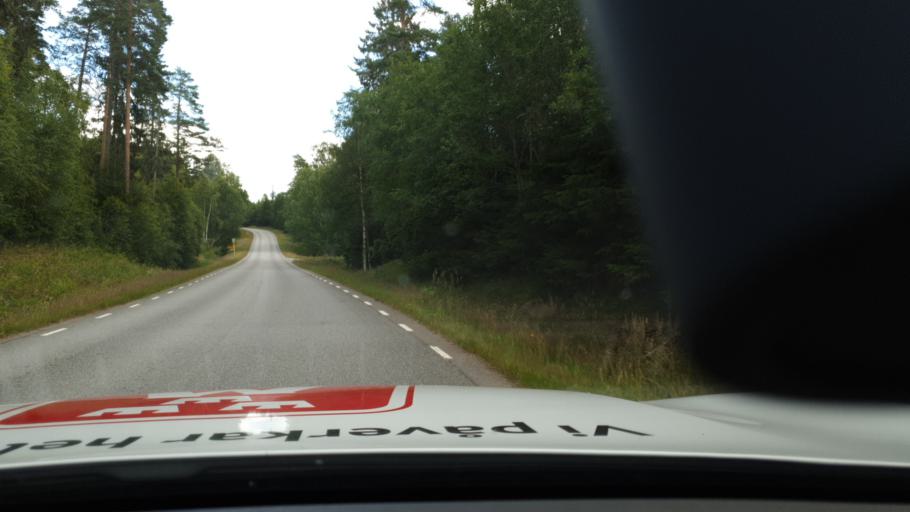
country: SE
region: Vaermland
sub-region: Kristinehamns Kommun
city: Bjorneborg
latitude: 59.3462
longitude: 14.2126
